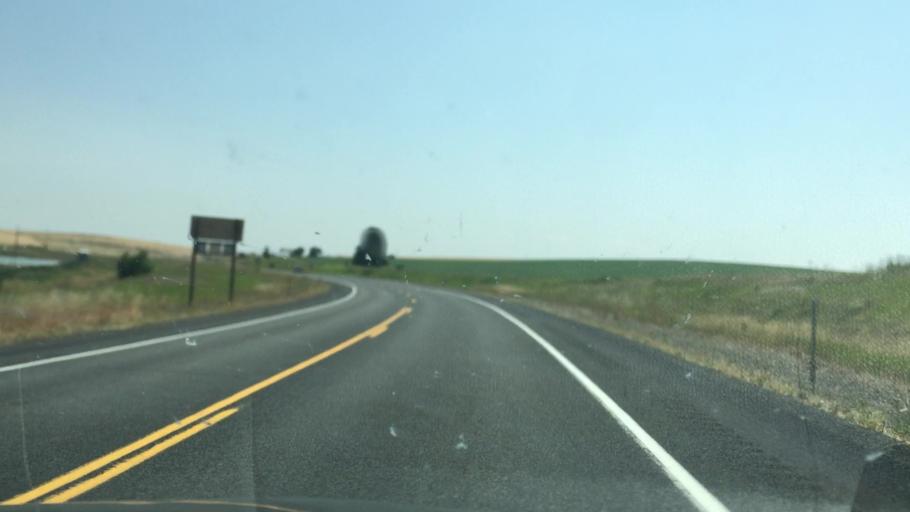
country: US
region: Idaho
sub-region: Lewis County
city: Nezperce
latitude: 46.2310
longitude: -116.4615
